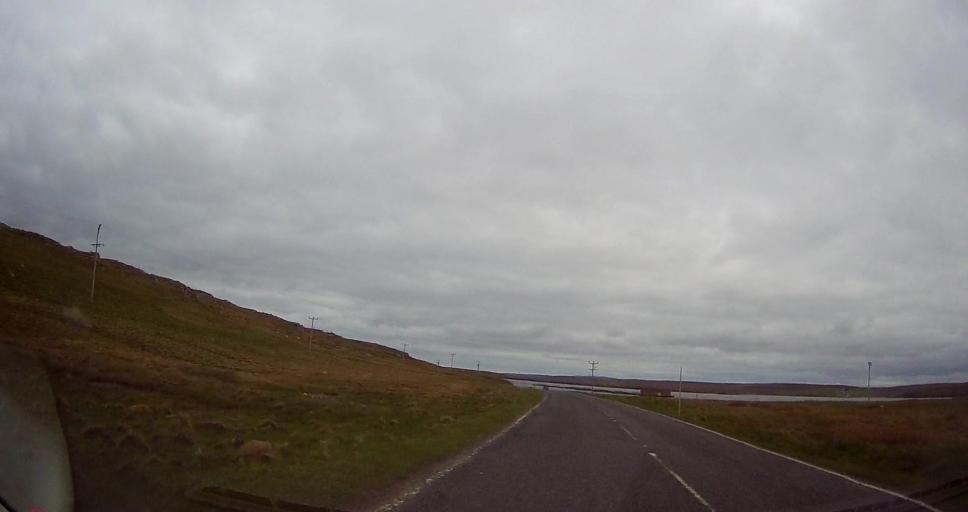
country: GB
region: Scotland
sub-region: Shetland Islands
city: Shetland
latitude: 60.6872
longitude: -0.9634
